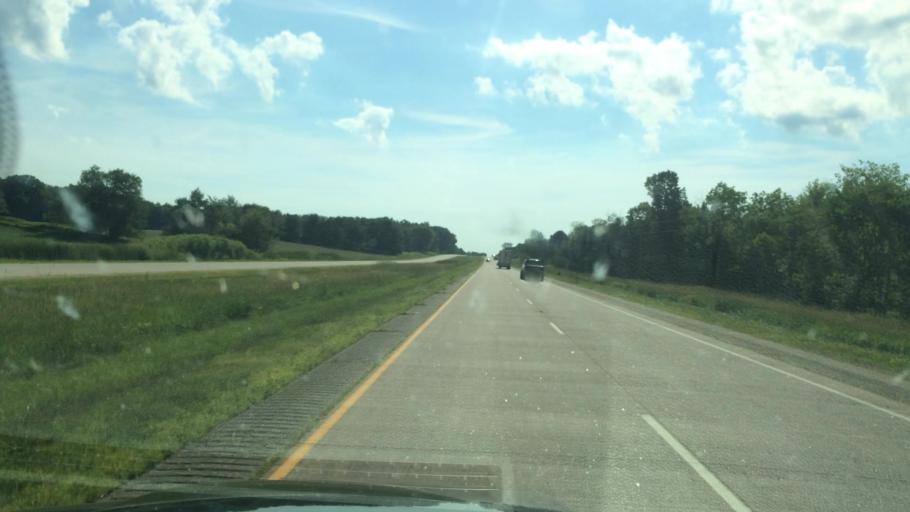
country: US
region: Wisconsin
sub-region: Waupaca County
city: Marion
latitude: 44.8040
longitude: -88.9892
